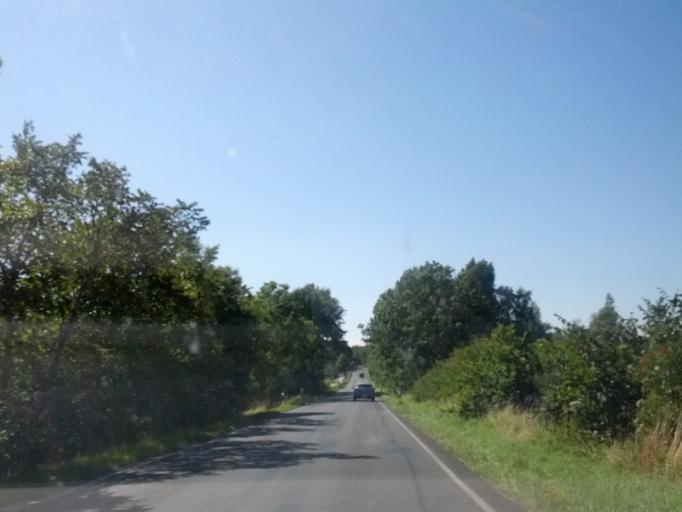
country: DE
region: Mecklenburg-Vorpommern
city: Bergen auf Ruegen
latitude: 54.4361
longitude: 13.4353
